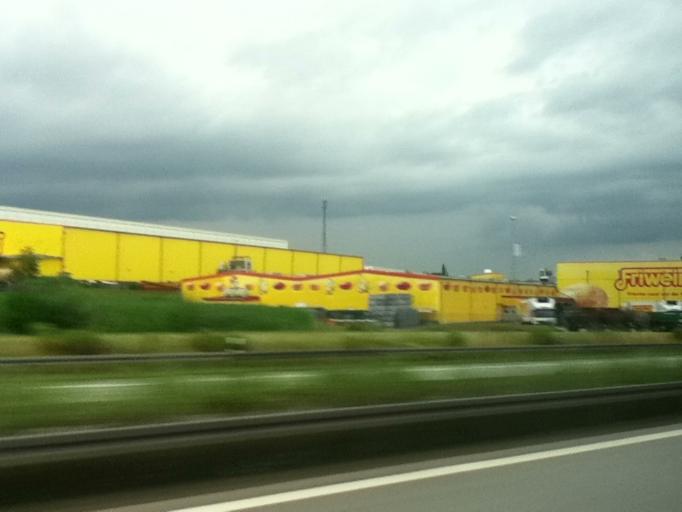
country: DE
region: Saxony
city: Pfaffroda
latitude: 50.8421
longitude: 12.5311
